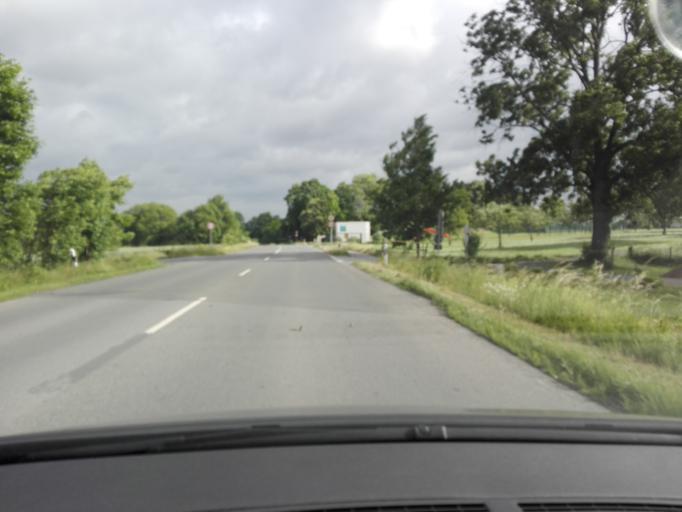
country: DE
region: North Rhine-Westphalia
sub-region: Regierungsbezirk Arnsberg
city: Unna
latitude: 51.5109
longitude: 7.7006
